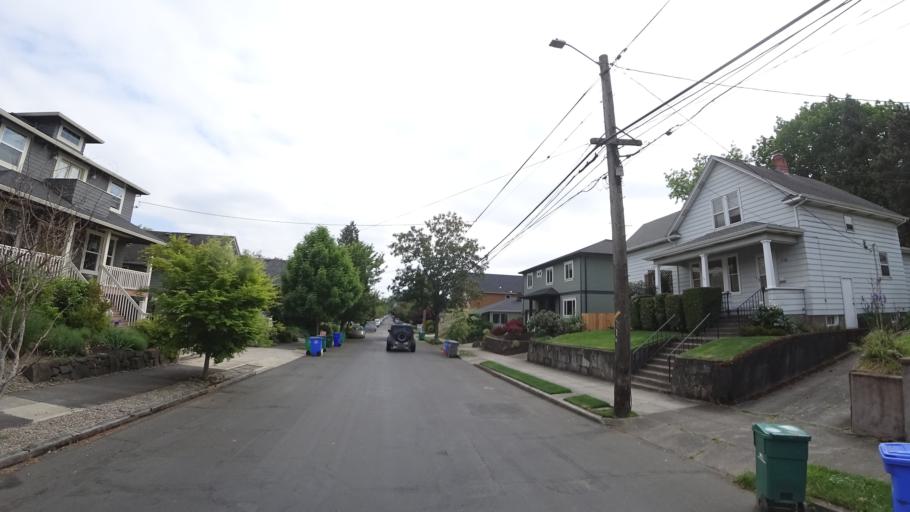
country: US
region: Oregon
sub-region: Multnomah County
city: Portland
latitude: 45.5516
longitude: -122.6518
